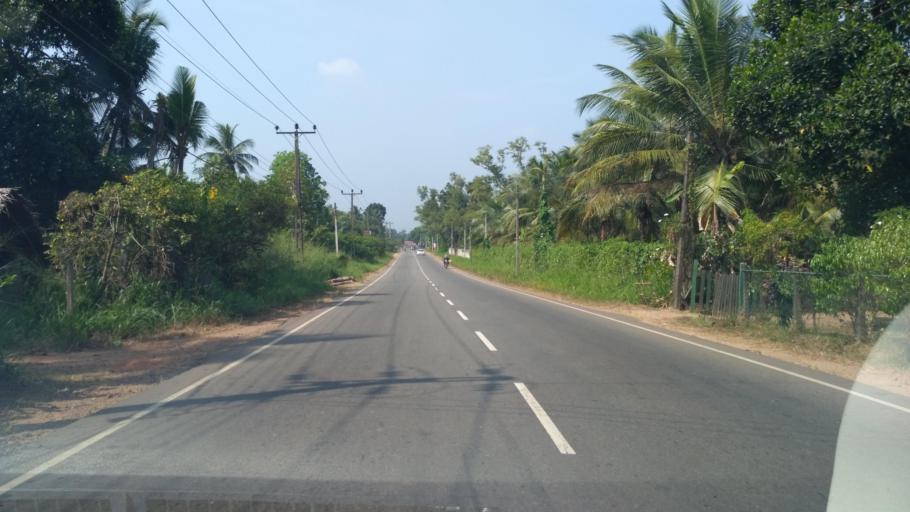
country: LK
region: North Western
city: Kuliyapitiya
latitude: 7.3323
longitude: 80.0009
